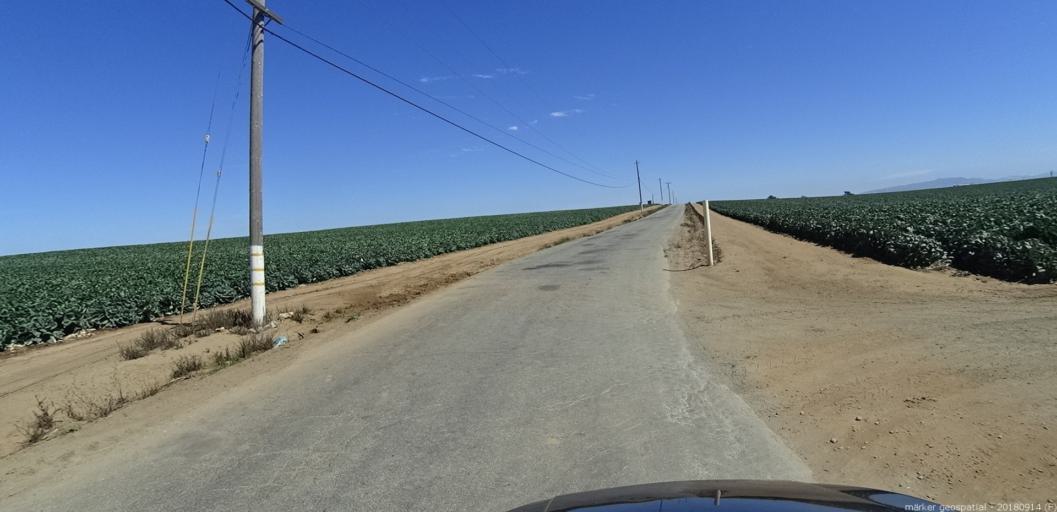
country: US
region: California
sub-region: Monterey County
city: Las Lomas
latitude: 36.8537
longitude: -121.7801
